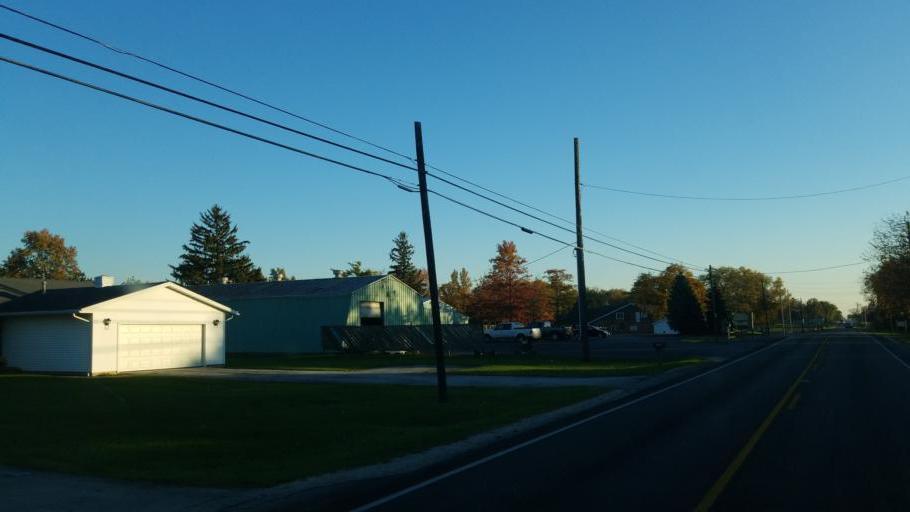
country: US
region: Ohio
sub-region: Sandusky County
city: Clyde
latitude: 41.2757
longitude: -82.9752
